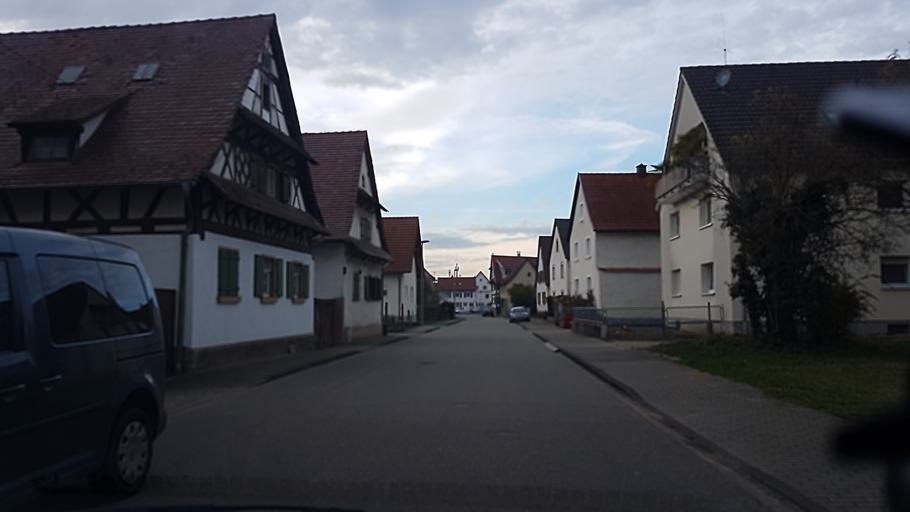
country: DE
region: Baden-Wuerttemberg
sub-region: Freiburg Region
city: Weisweil
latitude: 48.1974
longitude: 7.6771
